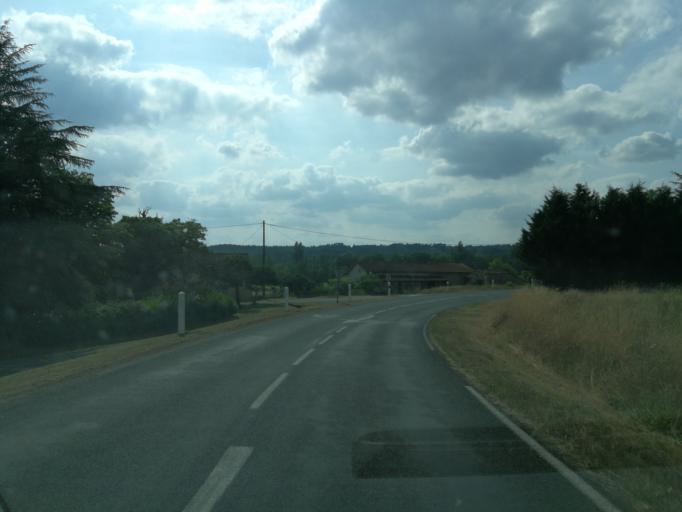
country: FR
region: Aquitaine
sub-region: Departement du Lot-et-Garonne
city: Fumel
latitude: 44.5238
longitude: 0.9478
